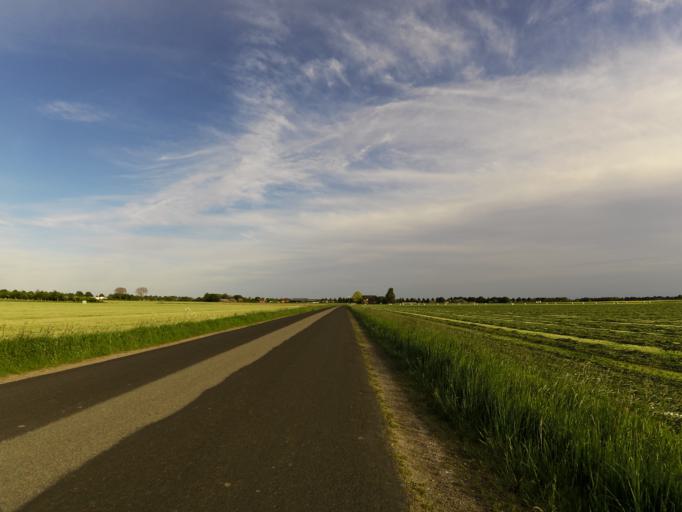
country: NL
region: Gelderland
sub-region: Gemeente Montferland
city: s-Heerenberg
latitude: 51.9071
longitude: 6.2992
